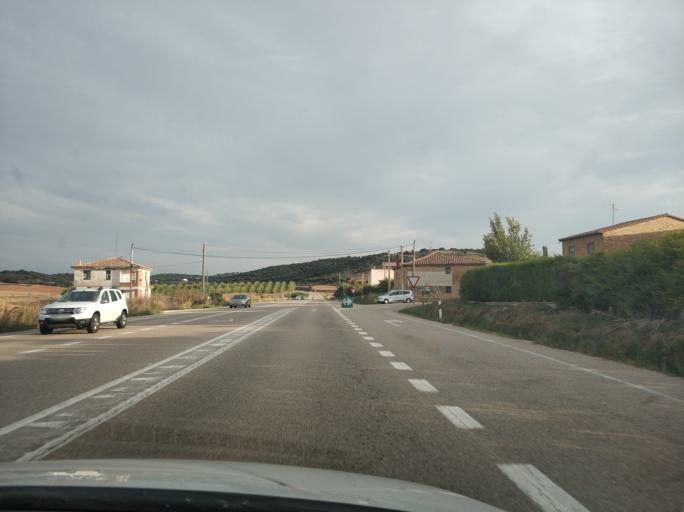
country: ES
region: Castille and Leon
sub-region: Provincia de Burgos
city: Hontoria de la Cantera
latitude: 42.1902
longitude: -3.6414
